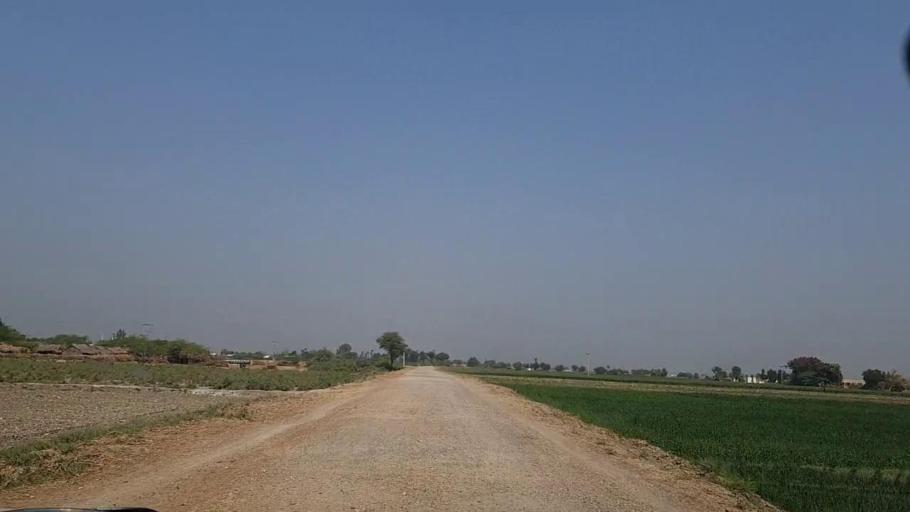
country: PK
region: Sindh
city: Mirpur Khas
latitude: 25.4958
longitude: 69.1913
